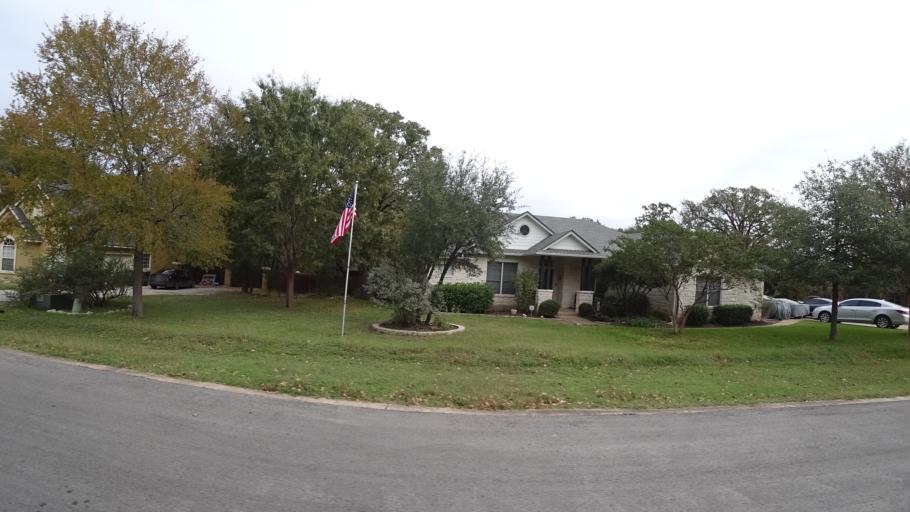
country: US
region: Texas
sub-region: Travis County
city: Shady Hollow
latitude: 30.1433
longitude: -97.8789
